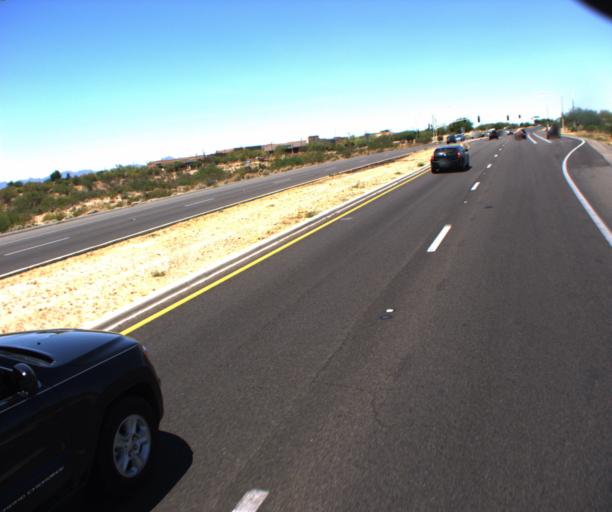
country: US
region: Arizona
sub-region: Pima County
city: Oro Valley
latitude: 32.4249
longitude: -110.9588
